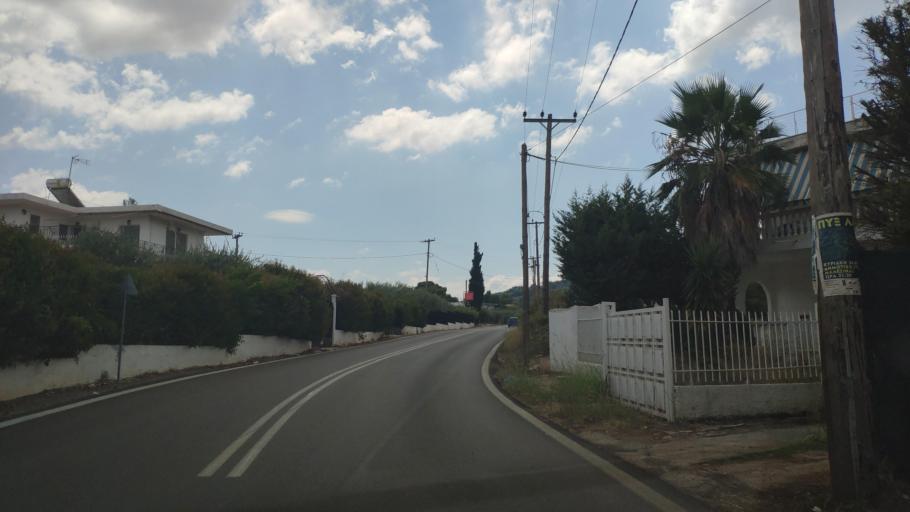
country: GR
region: Central Greece
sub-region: Nomos Fthiotidos
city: Malesina
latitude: 38.6516
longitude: 23.1966
